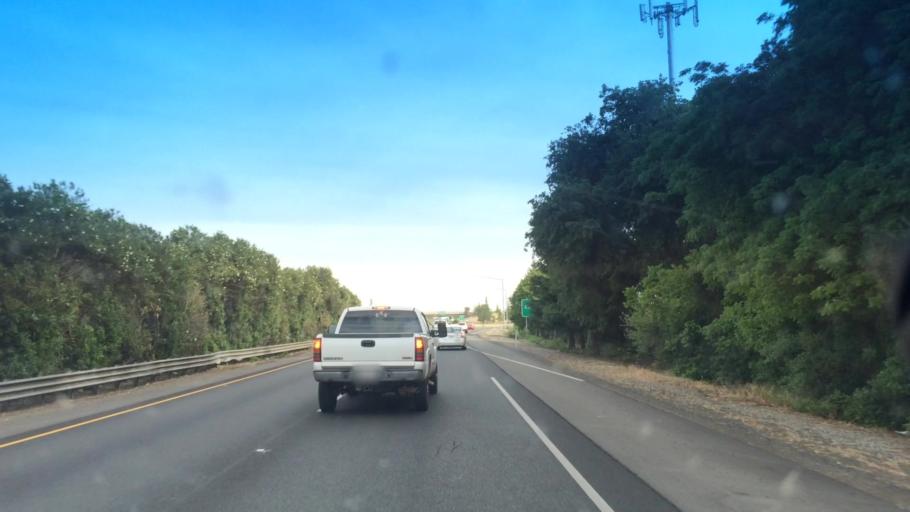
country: US
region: California
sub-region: Butte County
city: Chico
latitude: 39.7303
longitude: -121.8127
